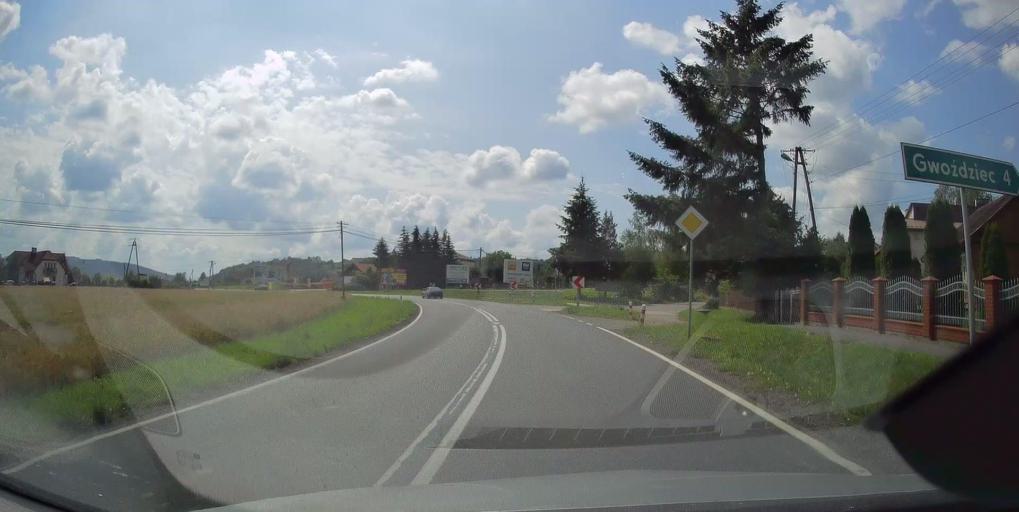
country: PL
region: Lesser Poland Voivodeship
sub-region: Powiat tarnowski
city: Zakliczyn
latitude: 49.8927
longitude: 20.8177
